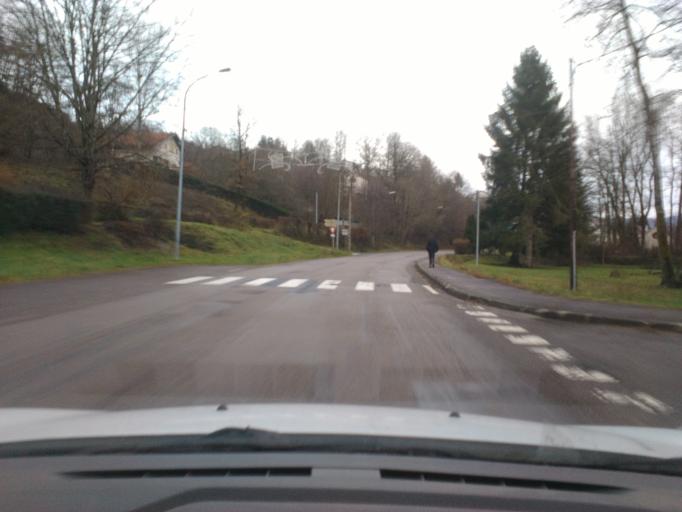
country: FR
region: Lorraine
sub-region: Departement des Vosges
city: Senones
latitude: 48.3924
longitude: 6.9640
